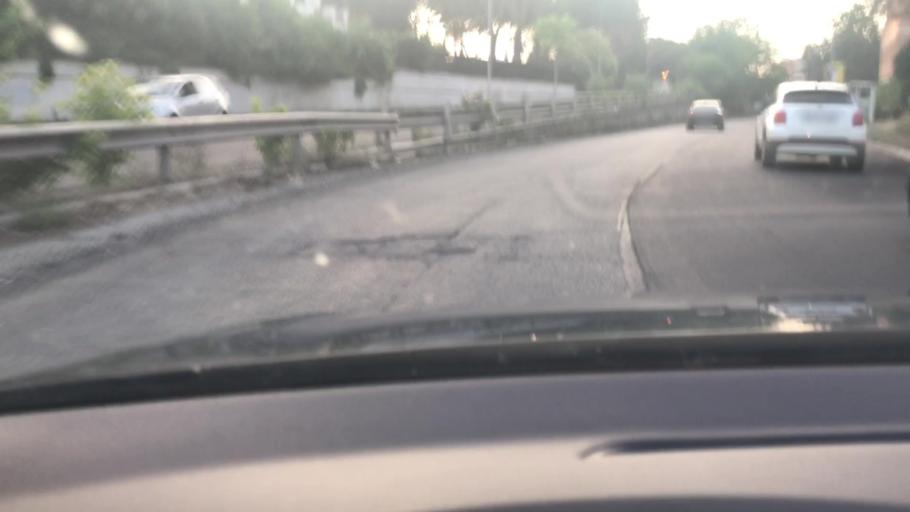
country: IT
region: Latium
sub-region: Citta metropolitana di Roma Capitale
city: Rome
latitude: 41.9283
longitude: 12.5636
